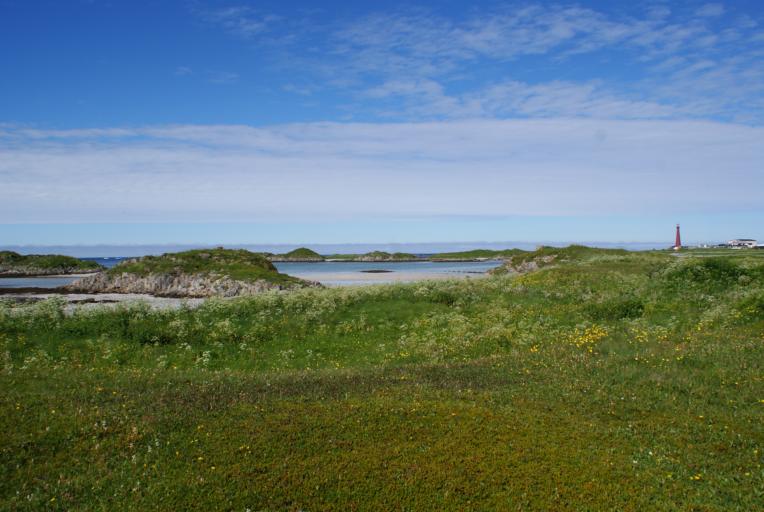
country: NO
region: Nordland
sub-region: Andoy
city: Andenes
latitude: 69.3136
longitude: 16.1072
